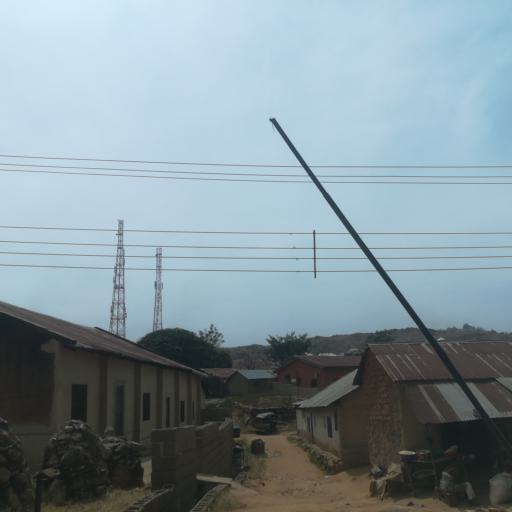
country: NG
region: Plateau
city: Jos
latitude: 9.9279
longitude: 8.8532
